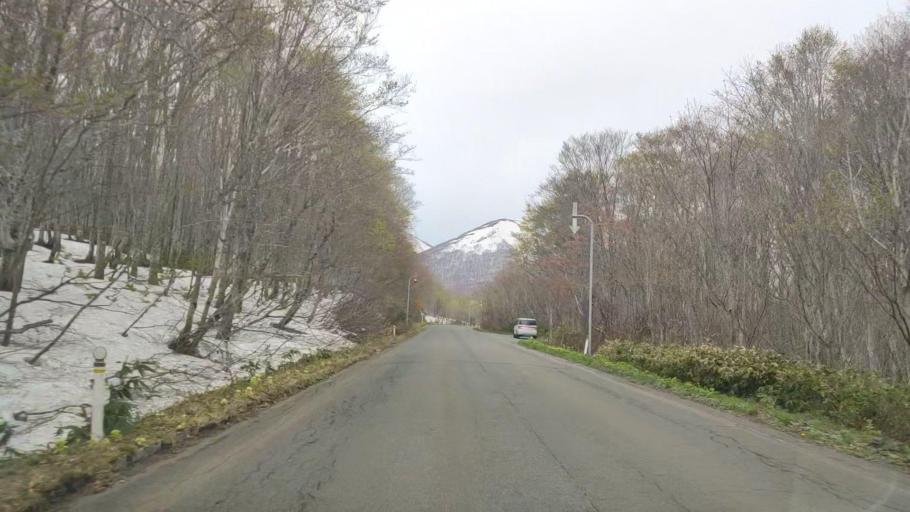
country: JP
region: Aomori
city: Aomori Shi
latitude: 40.6591
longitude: 140.9595
